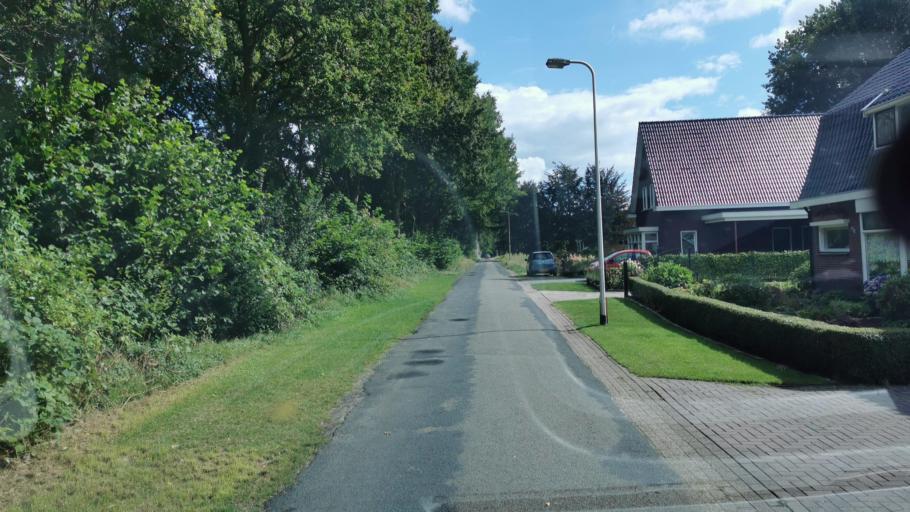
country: NL
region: Overijssel
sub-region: Gemeente Losser
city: Losser
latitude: 52.2620
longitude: 6.9941
